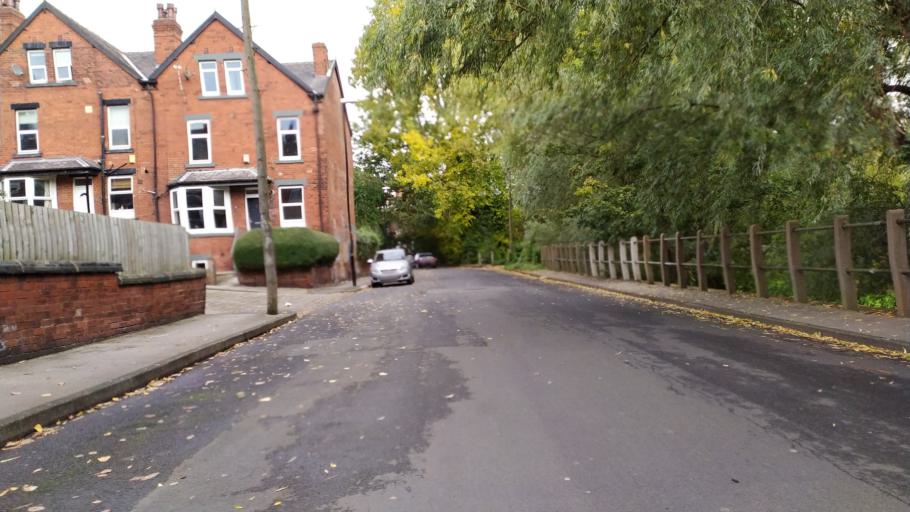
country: GB
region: England
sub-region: City and Borough of Leeds
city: Leeds
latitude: 53.8099
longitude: -1.5825
